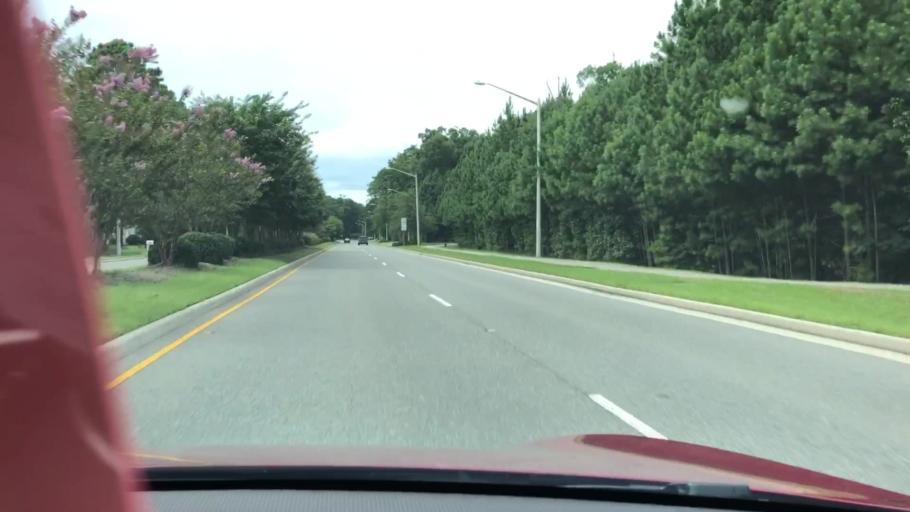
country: US
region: Virginia
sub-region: City of Virginia Beach
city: Virginia Beach
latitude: 36.8127
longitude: -75.9950
